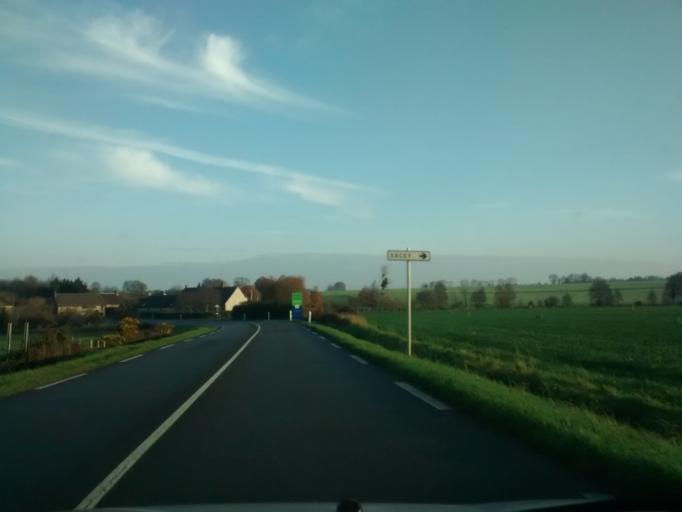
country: FR
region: Brittany
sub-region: Departement d'Ille-et-Vilaine
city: Antrain
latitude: 48.4863
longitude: -1.4674
